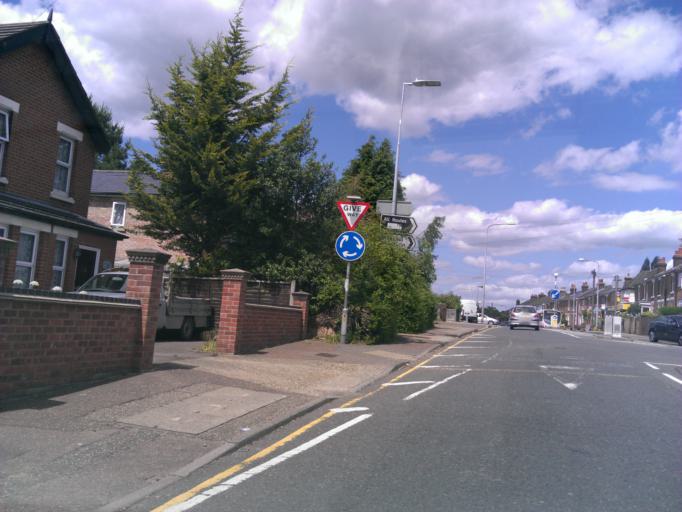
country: GB
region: England
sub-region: Essex
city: Colchester
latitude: 51.8731
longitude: 0.9245
